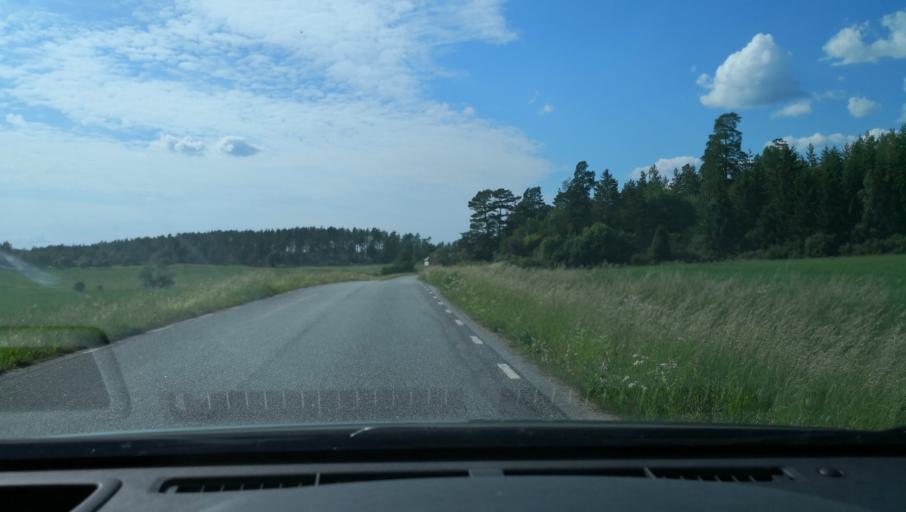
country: SE
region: Uppsala
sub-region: Enkopings Kommun
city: Orsundsbro
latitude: 59.8394
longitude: 17.2938
